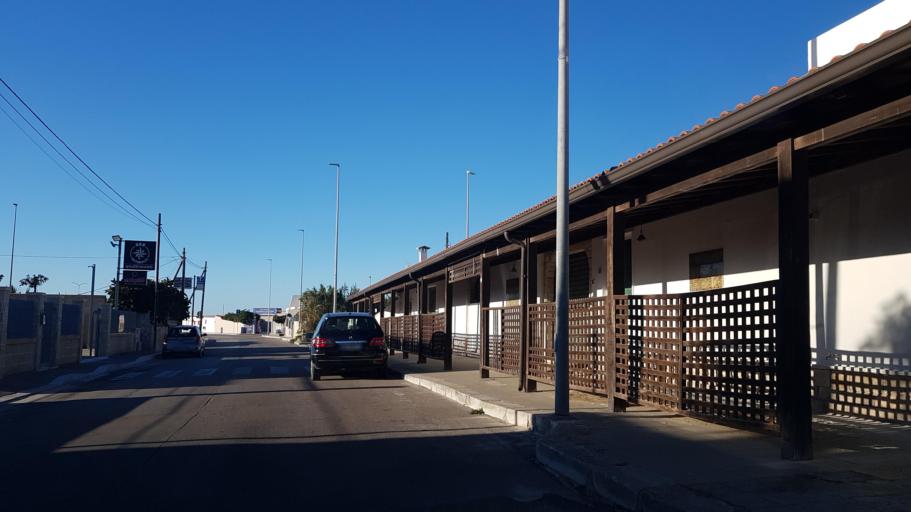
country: IT
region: Apulia
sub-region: Provincia di Lecce
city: Giorgilorio
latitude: 40.4664
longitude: 18.1951
